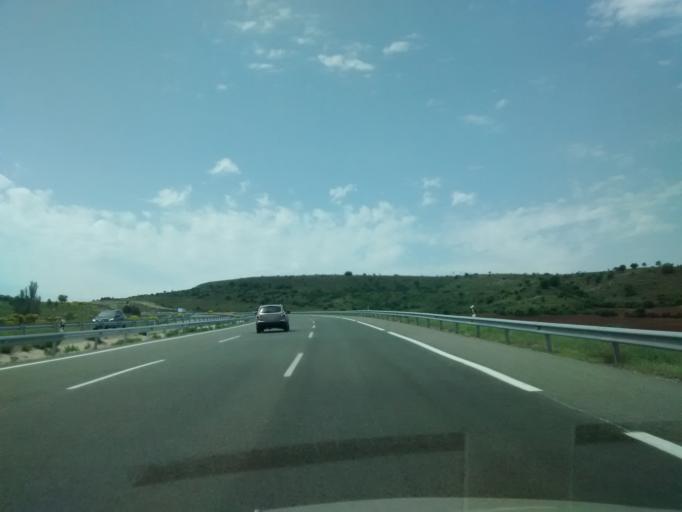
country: ES
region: Castille-La Mancha
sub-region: Provincia de Guadalajara
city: Alcolea del Pinar
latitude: 41.0582
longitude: -2.4475
